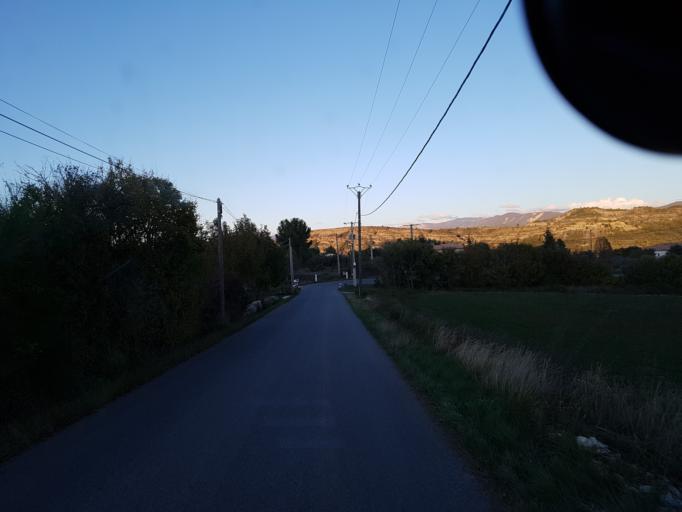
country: FR
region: Provence-Alpes-Cote d'Azur
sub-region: Departement des Alpes-de-Haute-Provence
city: Peipin
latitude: 44.0887
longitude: 5.9431
